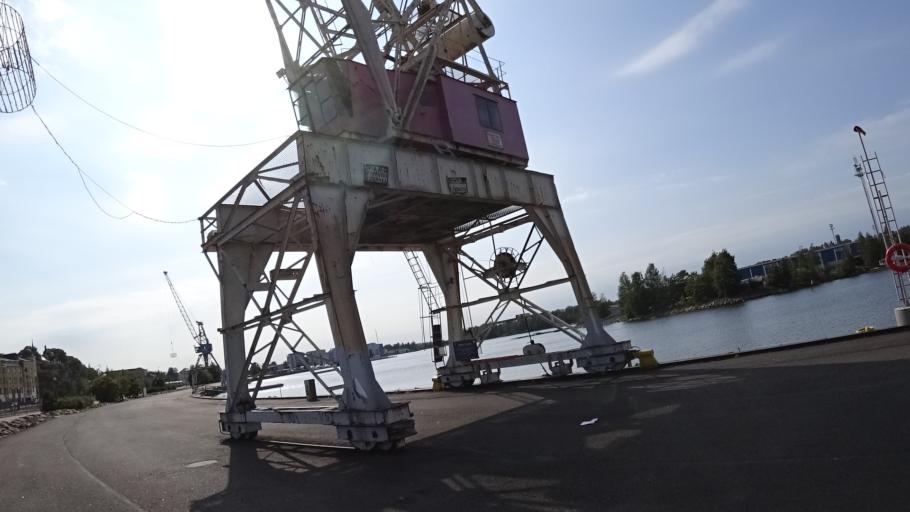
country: FI
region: Kymenlaakso
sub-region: Kotka-Hamina
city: Kotka
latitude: 60.4706
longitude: 26.9432
